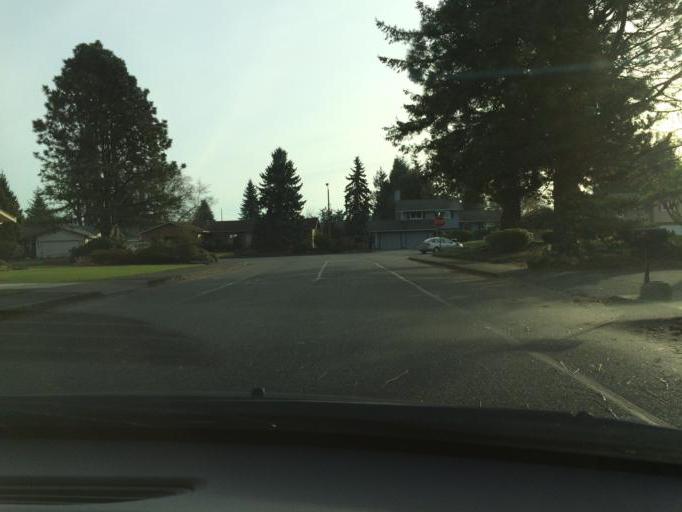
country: US
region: Washington
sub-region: Whatcom County
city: Lynden
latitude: 48.9524
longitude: -122.4350
